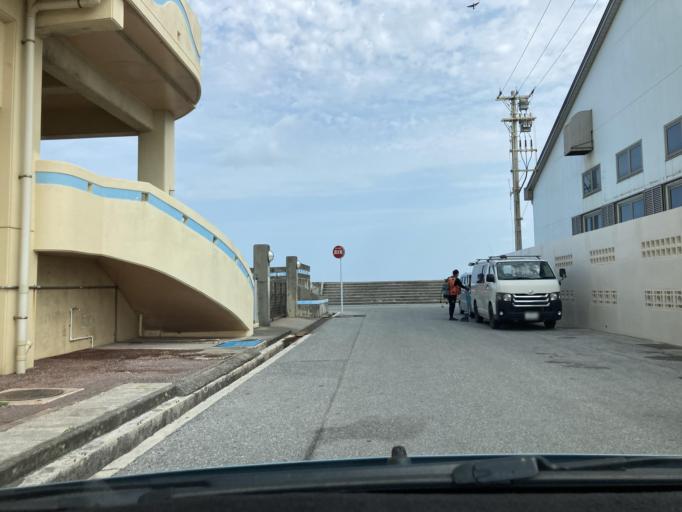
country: JP
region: Okinawa
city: Ginowan
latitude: 26.2742
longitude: 127.7141
